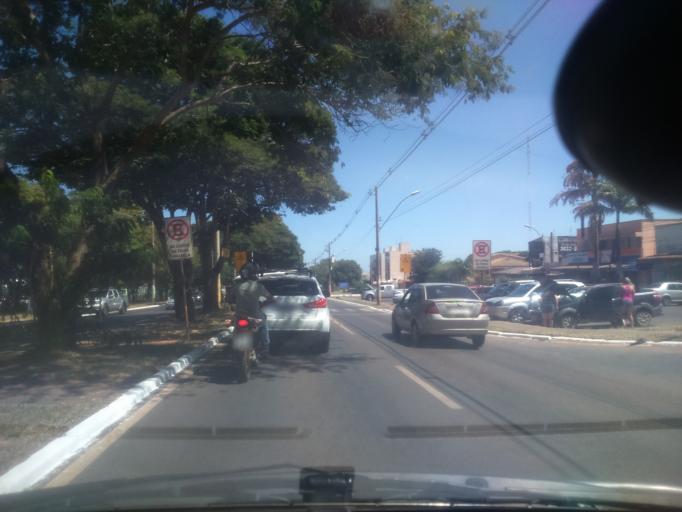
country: BR
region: Goias
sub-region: Luziania
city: Luziania
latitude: -16.0109
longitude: -48.0641
